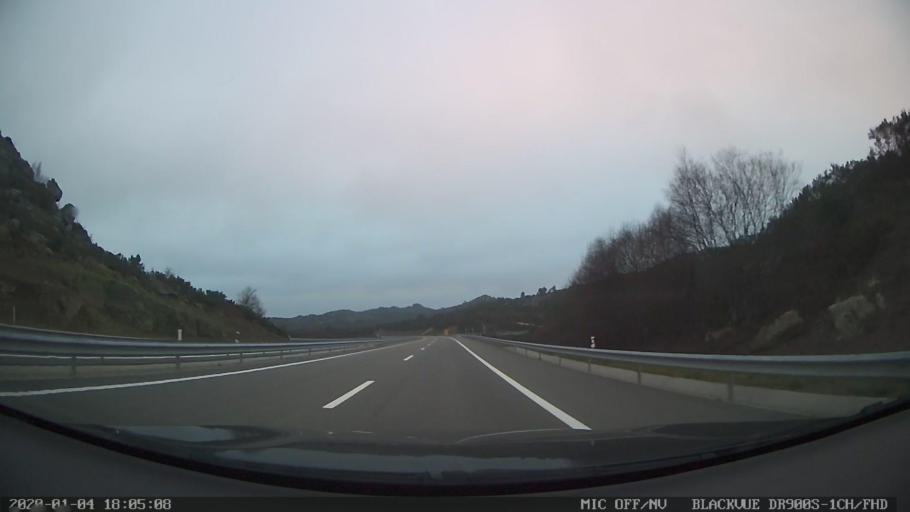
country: PT
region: Vila Real
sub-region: Vila Pouca de Aguiar
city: Vila Pouca de Aguiar
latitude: 41.4053
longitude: -7.6437
